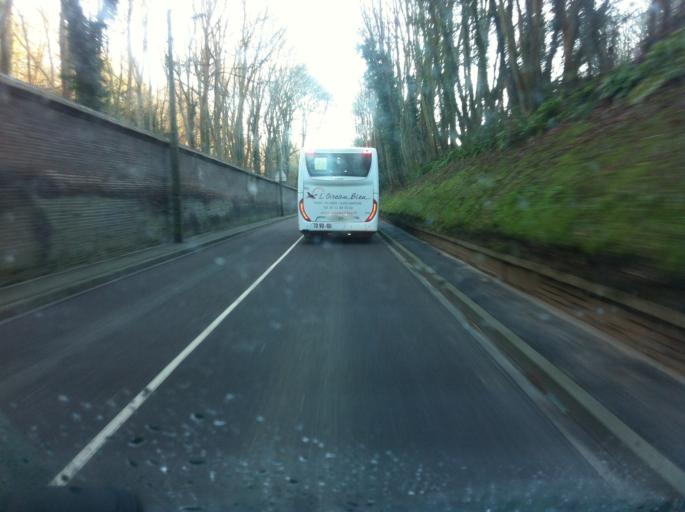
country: FR
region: Haute-Normandie
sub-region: Departement de la Seine-Maritime
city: Eu
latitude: 50.0490
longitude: 1.4086
